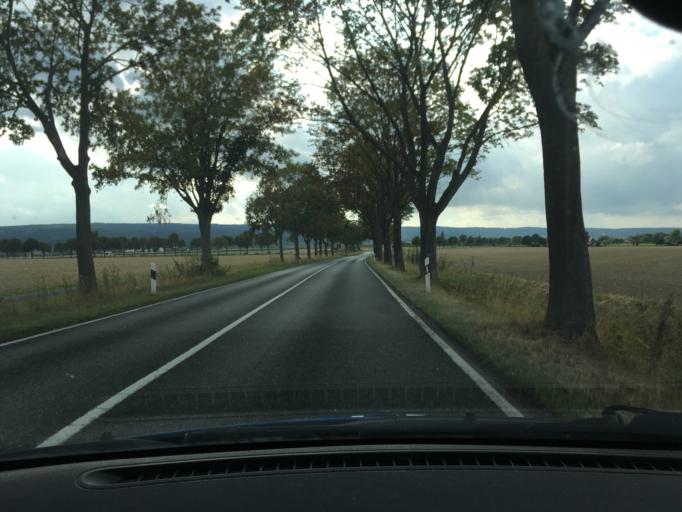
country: DE
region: Lower Saxony
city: Egestorf
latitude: 52.3015
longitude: 9.5197
